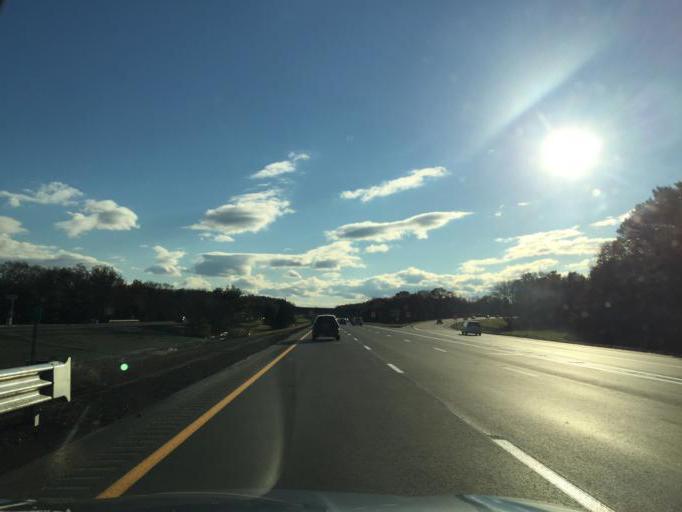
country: US
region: Massachusetts
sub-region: Bristol County
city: Attleboro
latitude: 41.9588
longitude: -71.3021
